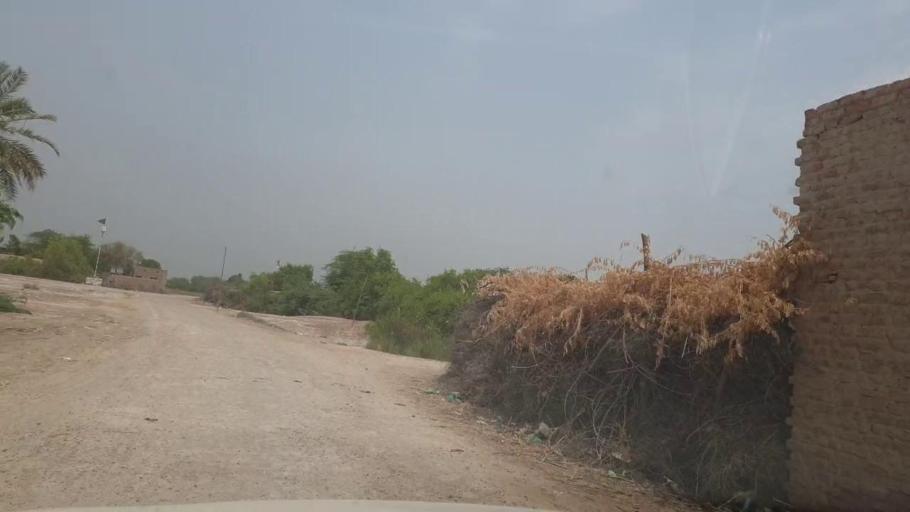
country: PK
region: Sindh
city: Kot Diji
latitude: 27.4390
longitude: 68.6453
